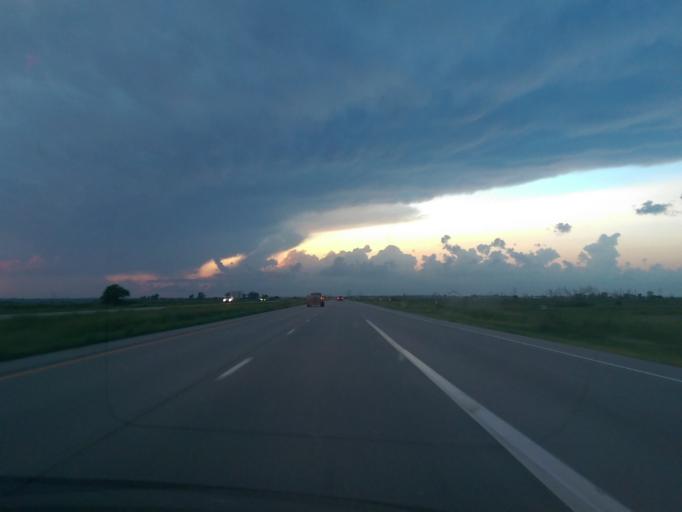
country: US
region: Nebraska
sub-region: Otoe County
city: Nebraska City
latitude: 40.7095
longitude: -95.7975
